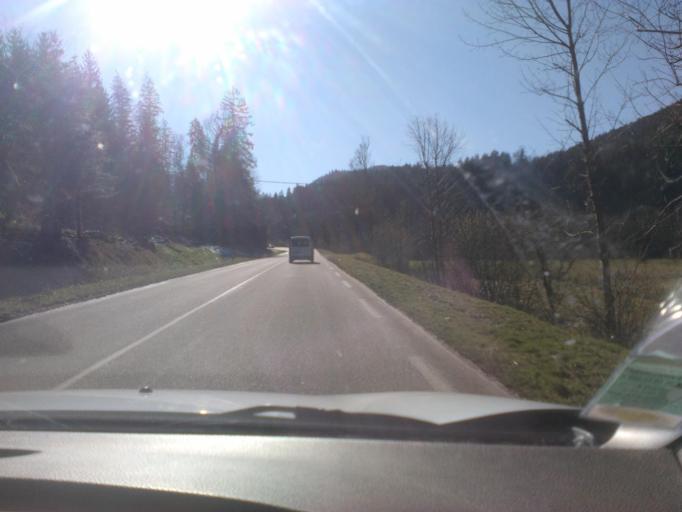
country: FR
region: Alsace
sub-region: Departement du Bas-Rhin
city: Rothau
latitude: 48.3833
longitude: 7.1430
